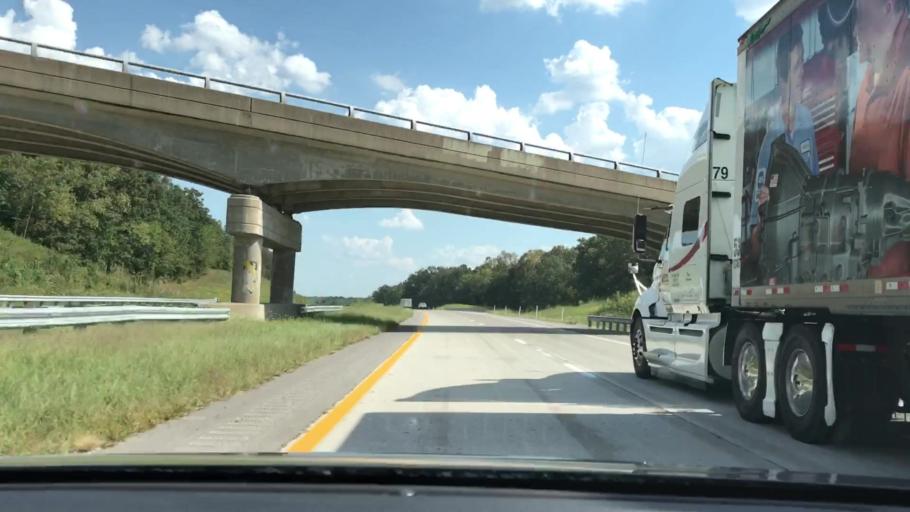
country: US
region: Kentucky
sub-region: Ohio County
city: Oak Grove
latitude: 37.3509
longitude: -86.7850
